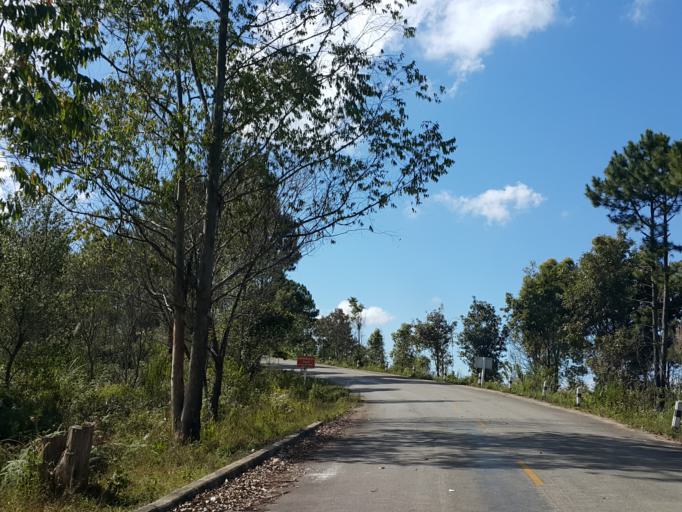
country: TH
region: Chiang Mai
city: Wiang Haeng
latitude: 19.5192
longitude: 98.7597
